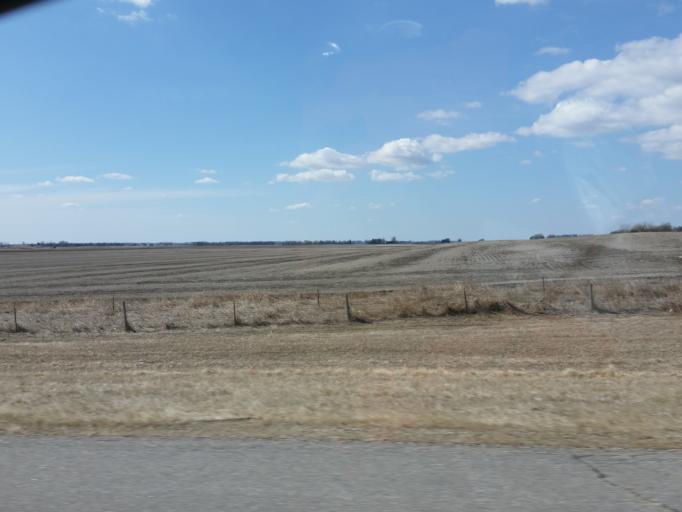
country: US
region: South Dakota
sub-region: Codington County
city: Watertown
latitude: 45.0448
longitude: -97.0552
